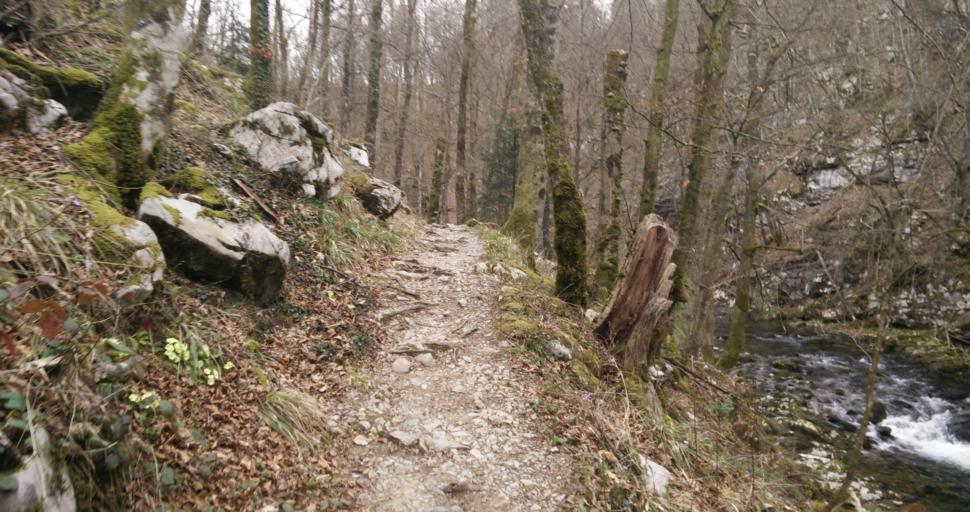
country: HR
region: Primorsko-Goranska
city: Vrbovsko
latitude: 45.3632
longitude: 15.0678
